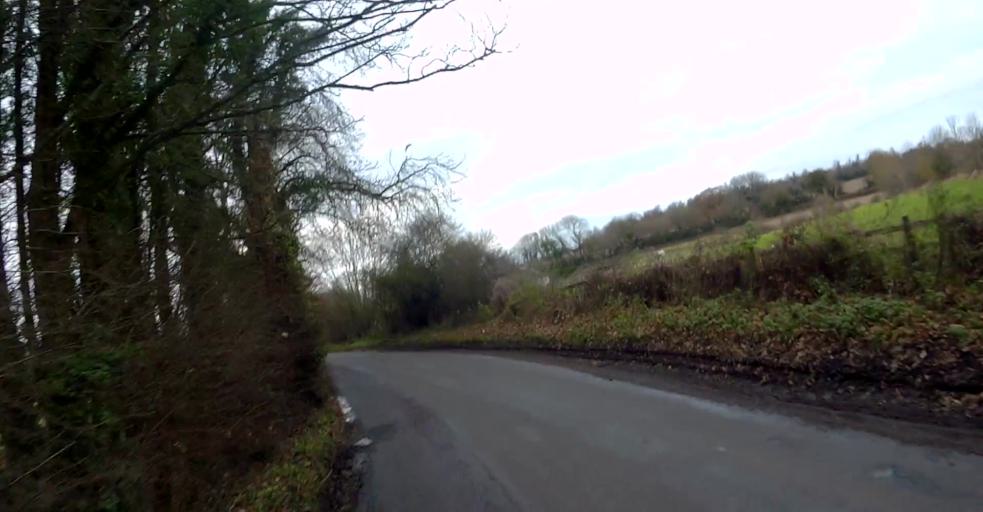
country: GB
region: England
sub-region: Hampshire
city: Overton
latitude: 51.2006
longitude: -1.1719
